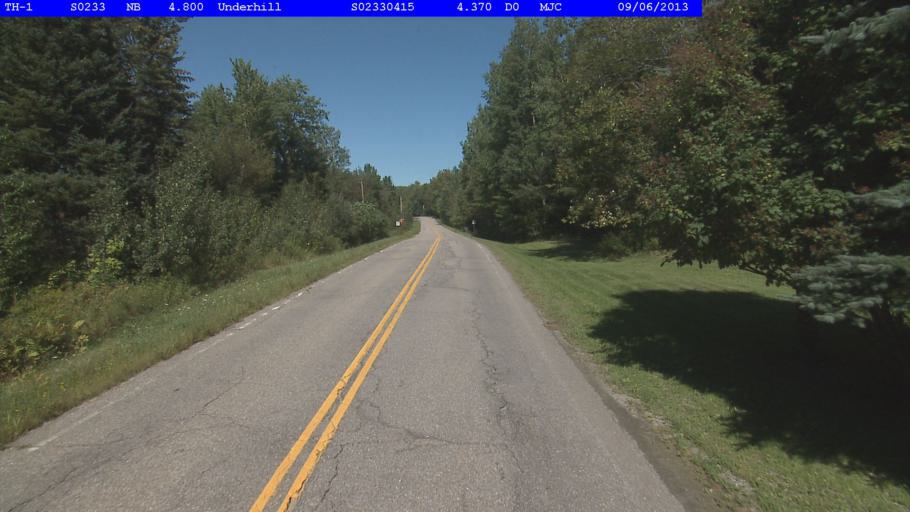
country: US
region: Vermont
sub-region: Chittenden County
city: Jericho
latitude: 44.5294
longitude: -72.8766
